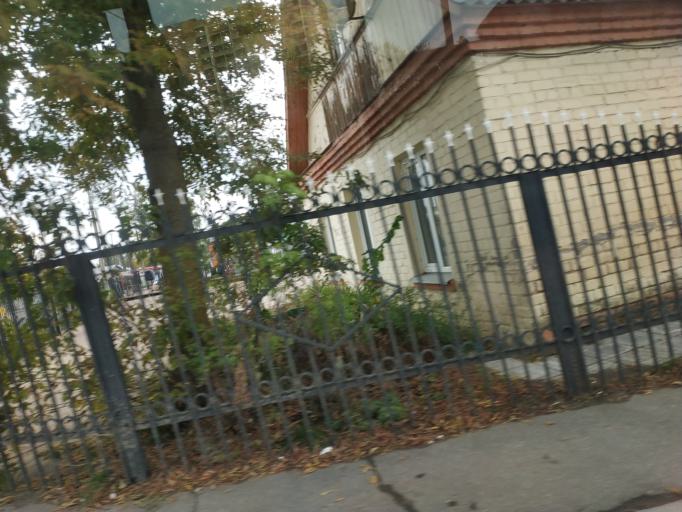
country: RU
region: Moskovskaya
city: Mozhaysk
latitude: 55.4962
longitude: 36.0297
